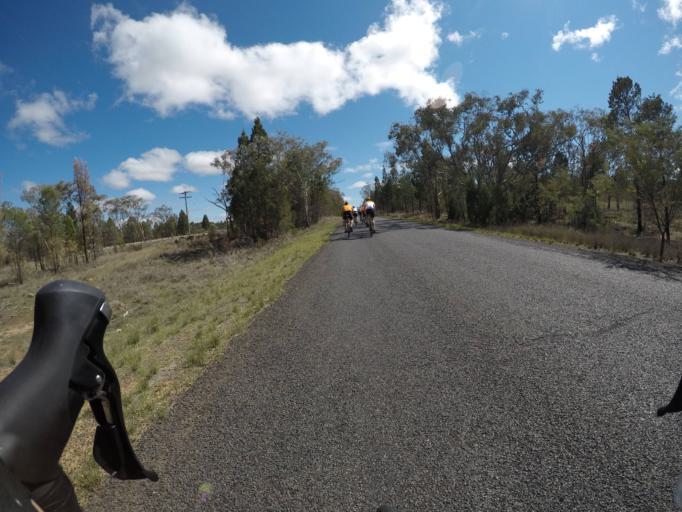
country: AU
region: New South Wales
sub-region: Parkes
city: Peak Hill
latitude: -32.6315
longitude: 148.5493
